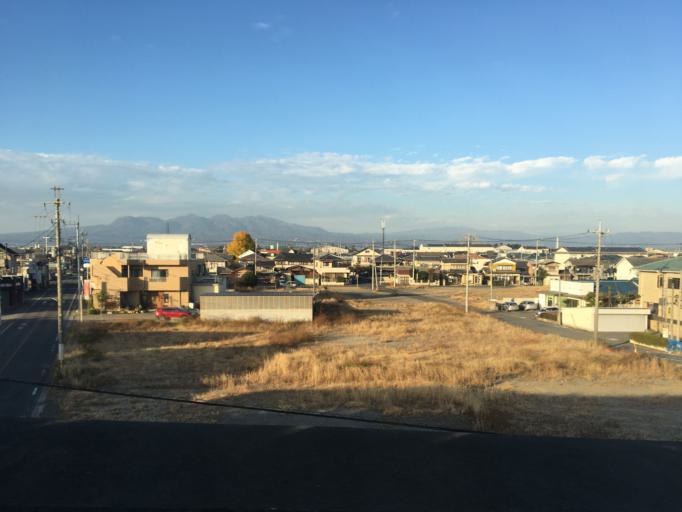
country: JP
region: Gunma
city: Isesaki
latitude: 36.3274
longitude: 139.1911
